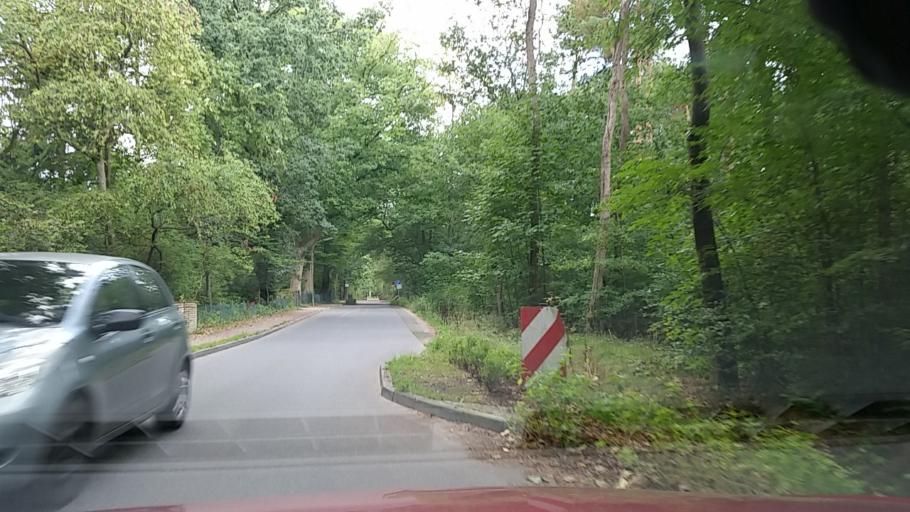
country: DE
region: Schleswig-Holstein
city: Wedel
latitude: 53.5949
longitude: 9.7464
